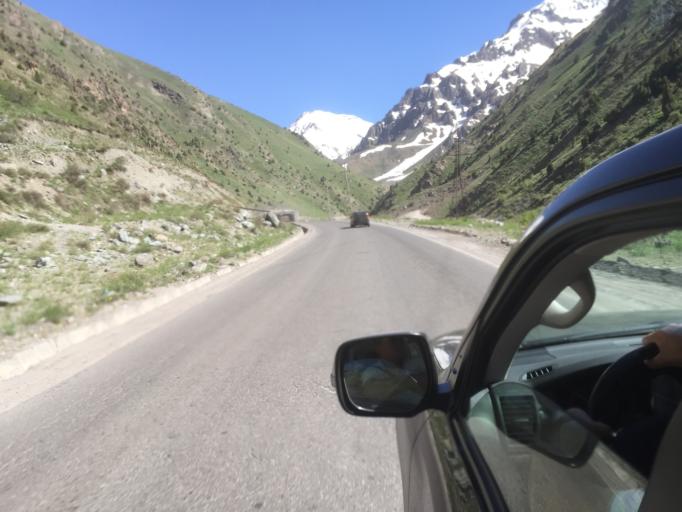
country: TJ
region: Viloyati Sughd
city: Ayni
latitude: 39.1208
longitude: 68.6851
